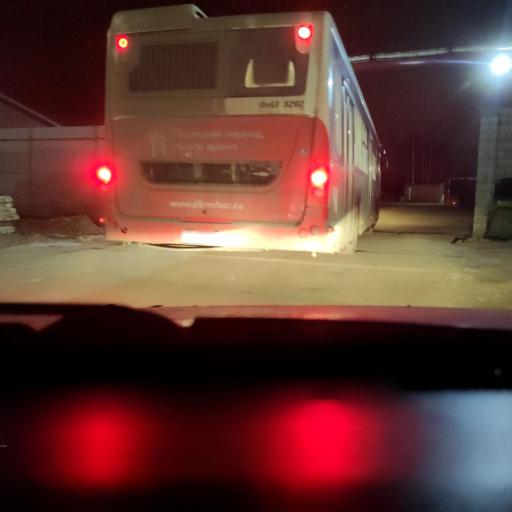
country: RU
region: Perm
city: Kondratovo
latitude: 57.9525
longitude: 56.0888
